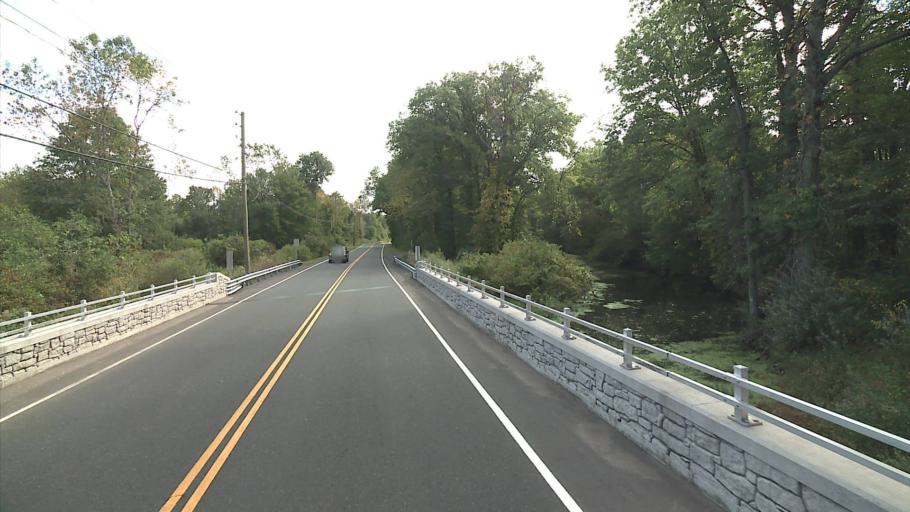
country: US
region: Connecticut
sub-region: Middlesex County
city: Durham
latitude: 41.4954
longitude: -72.7051
